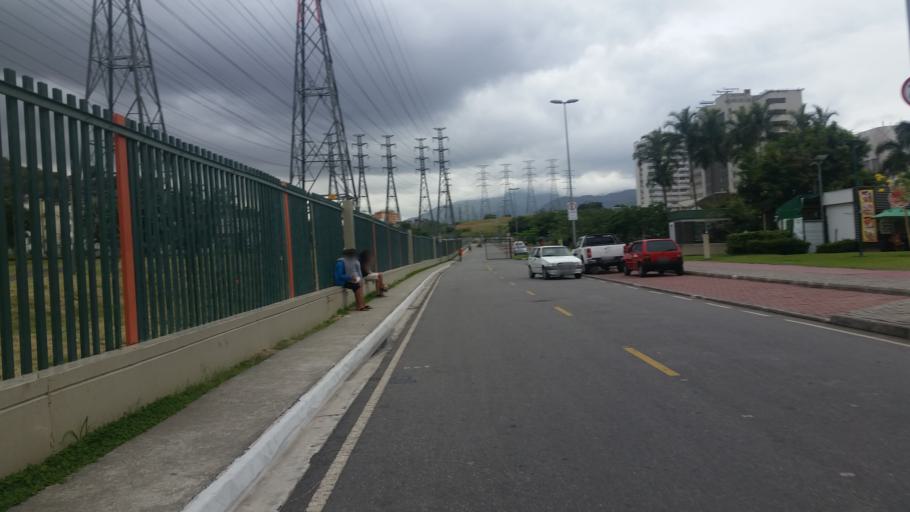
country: BR
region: Rio de Janeiro
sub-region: Sao Joao De Meriti
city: Sao Joao de Meriti
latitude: -22.8677
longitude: -43.3414
